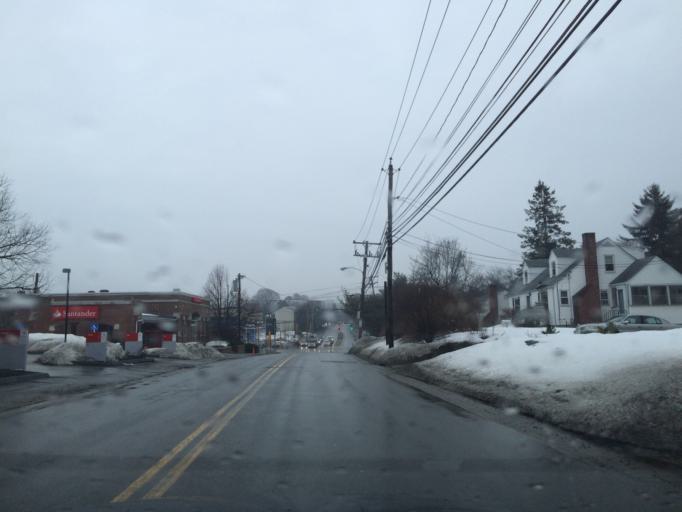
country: US
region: Massachusetts
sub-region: Middlesex County
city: Waltham
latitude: 42.4114
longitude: -71.2356
